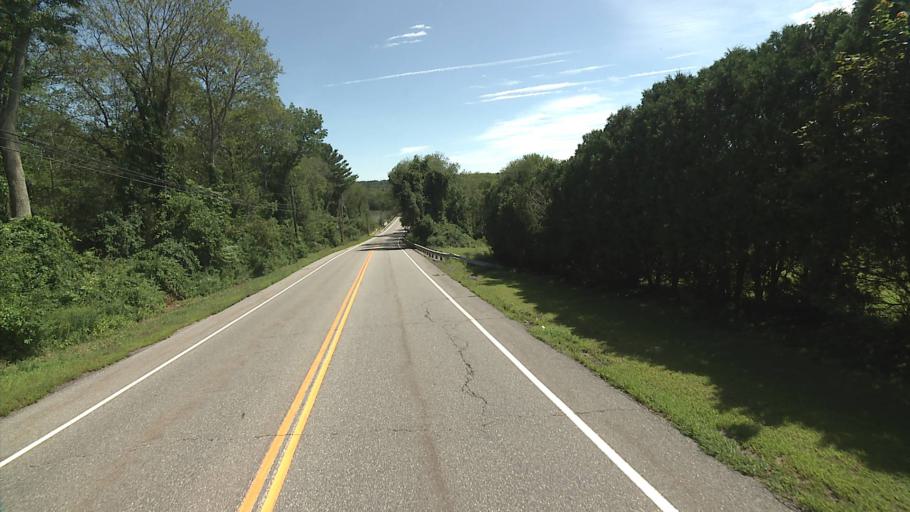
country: US
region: Rhode Island
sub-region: Providence County
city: Foster
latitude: 41.8490
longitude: -71.8138
